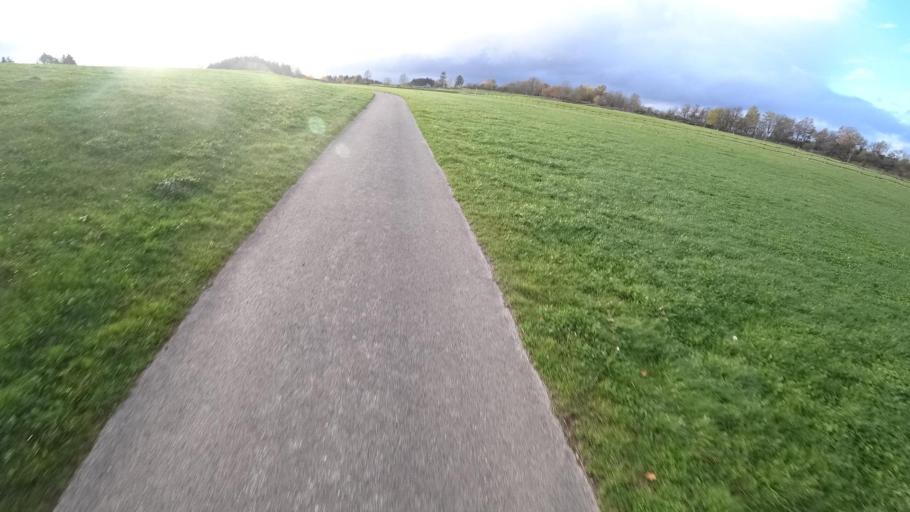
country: DE
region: Rheinland-Pfalz
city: Harscheid
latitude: 50.4620
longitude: 6.8931
